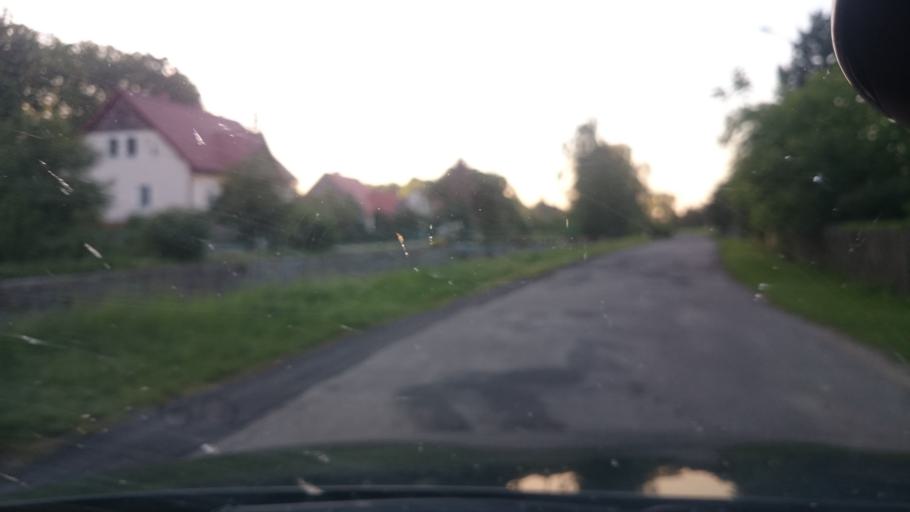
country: PL
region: Lower Silesian Voivodeship
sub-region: Powiat zabkowicki
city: Zloty Stok
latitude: 50.4663
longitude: 16.8464
